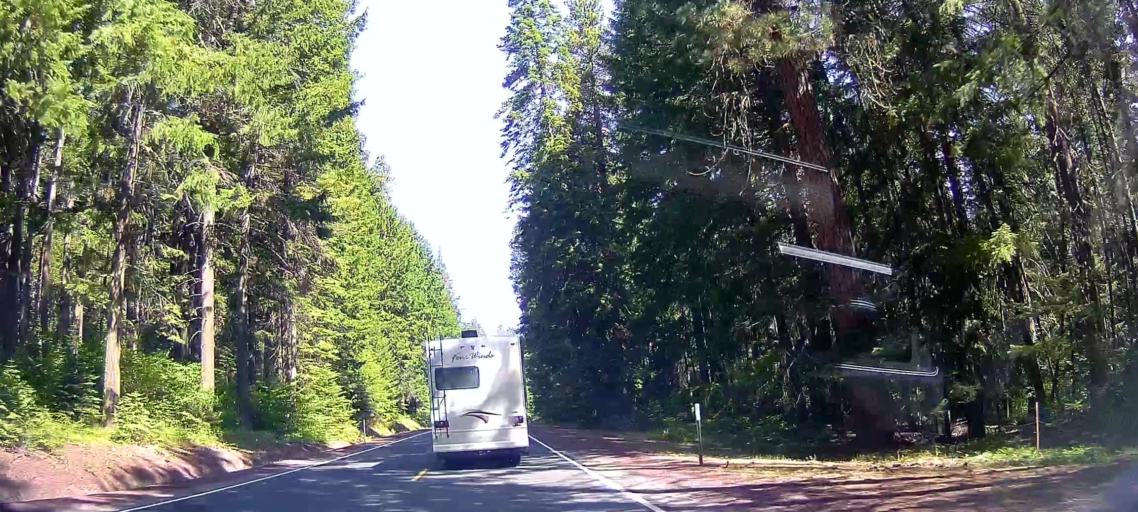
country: US
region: Oregon
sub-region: Jefferson County
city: Warm Springs
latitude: 45.0816
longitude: -121.5417
